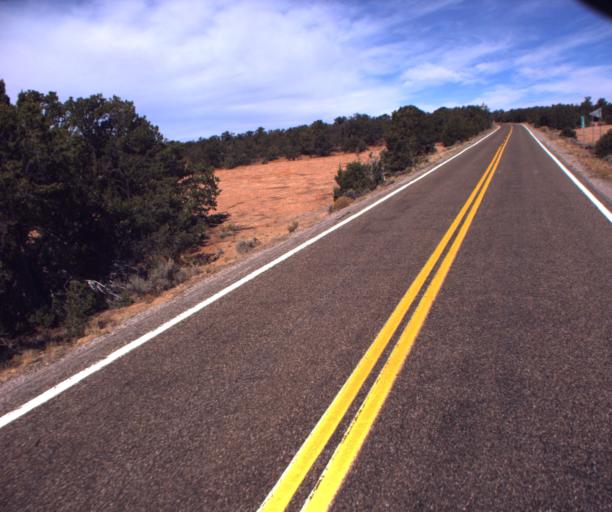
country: US
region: Arizona
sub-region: Navajo County
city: Kayenta
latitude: 36.6347
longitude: -110.5098
